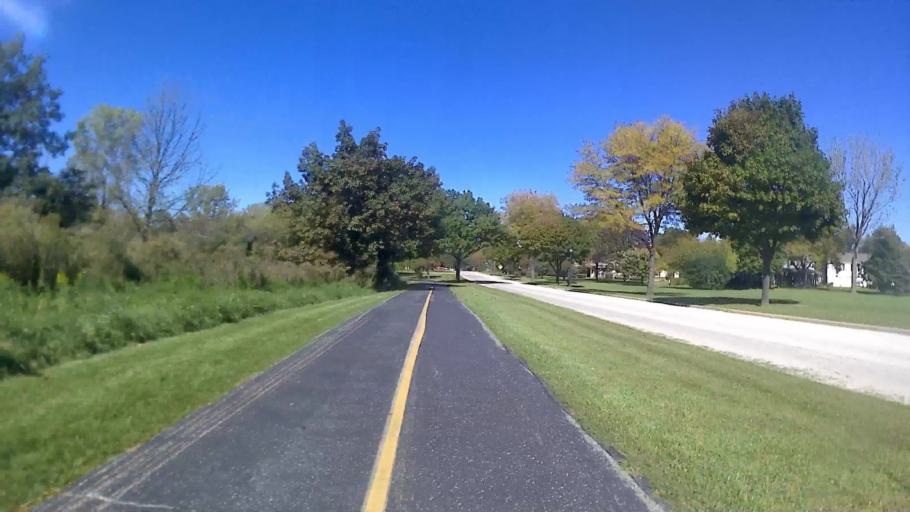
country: US
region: Illinois
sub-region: DuPage County
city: Itasca
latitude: 42.0080
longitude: -88.0188
